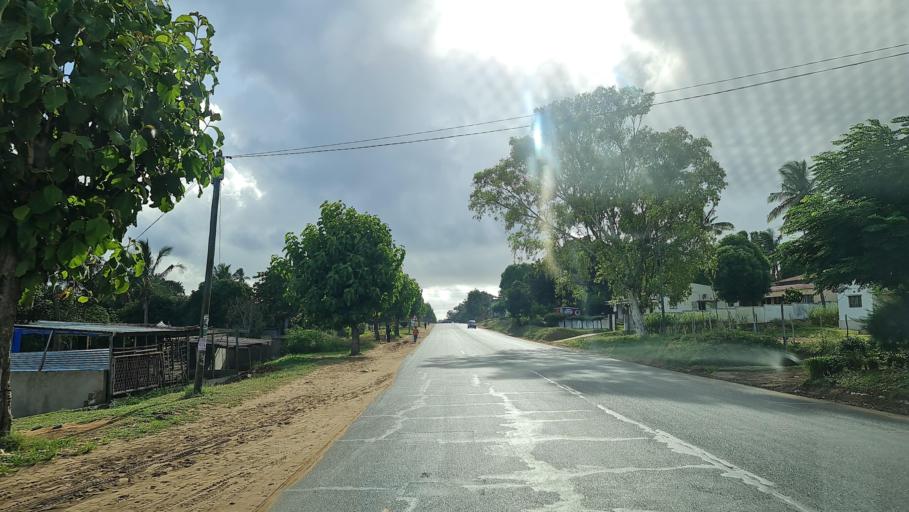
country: MZ
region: Gaza
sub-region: Xai-Xai District
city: Xai-Xai
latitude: -25.0562
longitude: 33.6872
